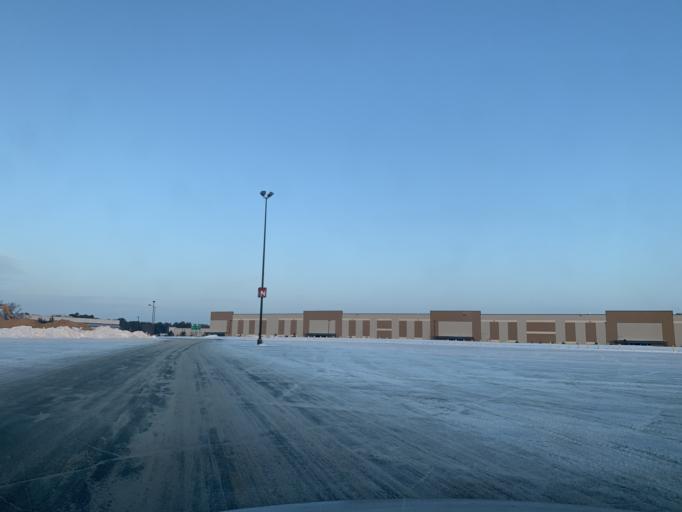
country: US
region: Minnesota
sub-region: Scott County
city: Shakopee
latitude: 44.7927
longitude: -93.4861
